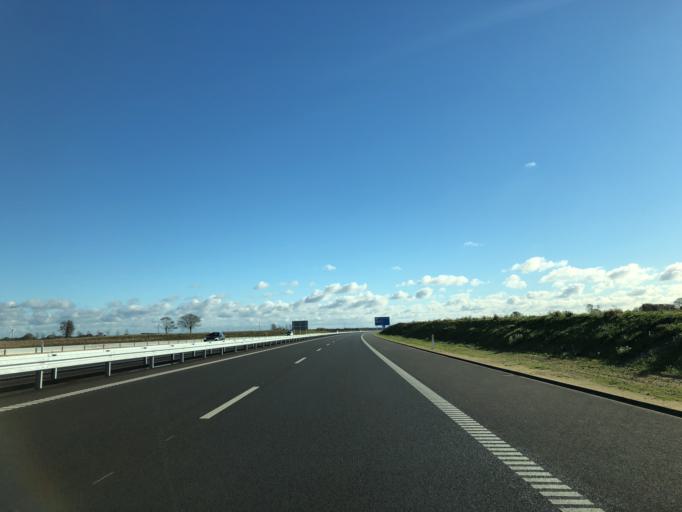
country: DK
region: Central Jutland
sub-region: Holstebro Kommune
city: Holstebro
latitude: 56.3758
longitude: 8.7015
